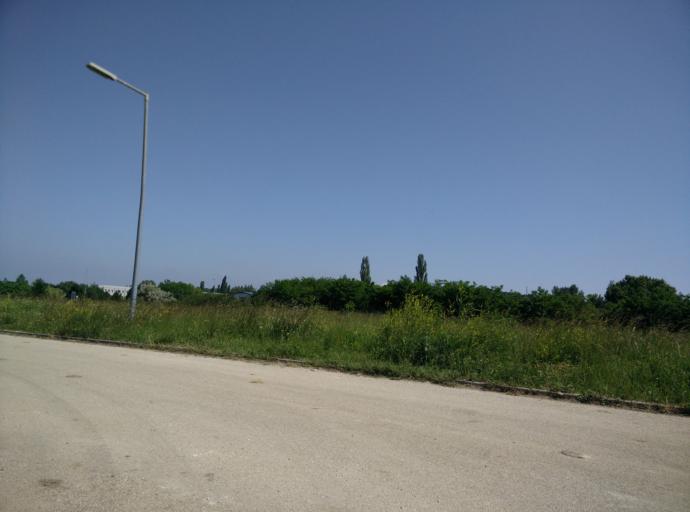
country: HU
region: Pest
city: Biatorbagy
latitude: 47.4731
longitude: 18.8405
